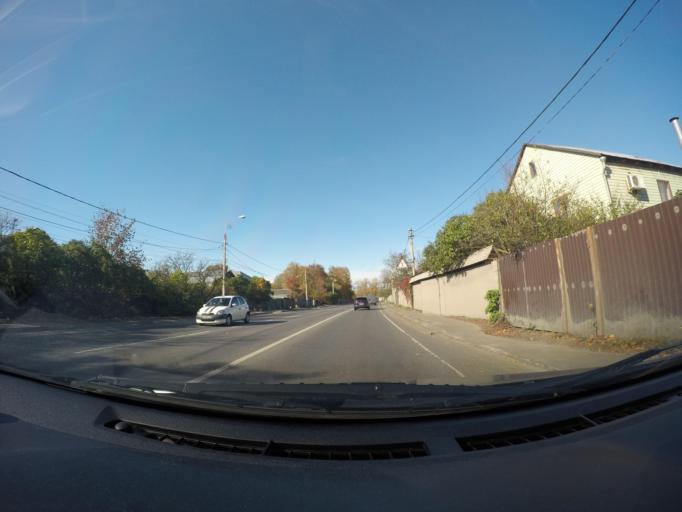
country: RU
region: Moskovskaya
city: Kraskovo
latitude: 55.6324
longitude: 37.9712
